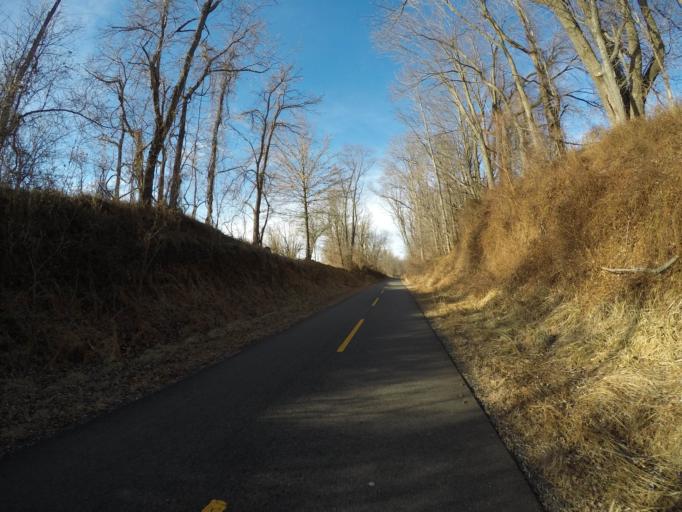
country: US
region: Virginia
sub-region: Loudoun County
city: Leesburg
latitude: 39.1185
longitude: -77.6027
